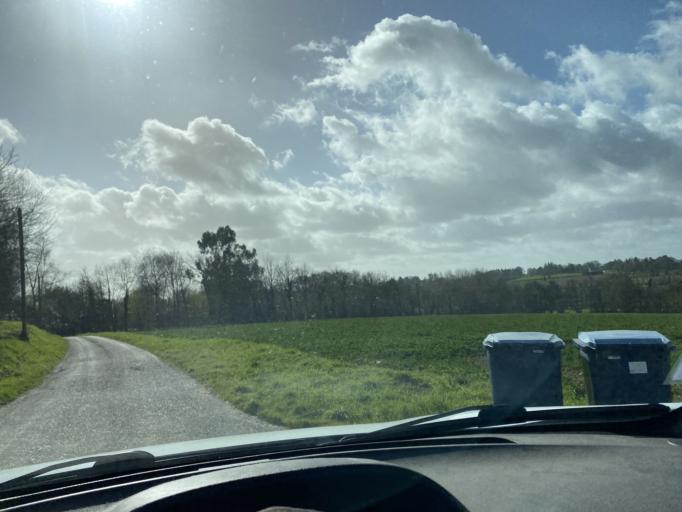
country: FR
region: Brittany
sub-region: Departement d'Ille-et-Vilaine
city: Melesse
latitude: 48.2086
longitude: -1.6904
